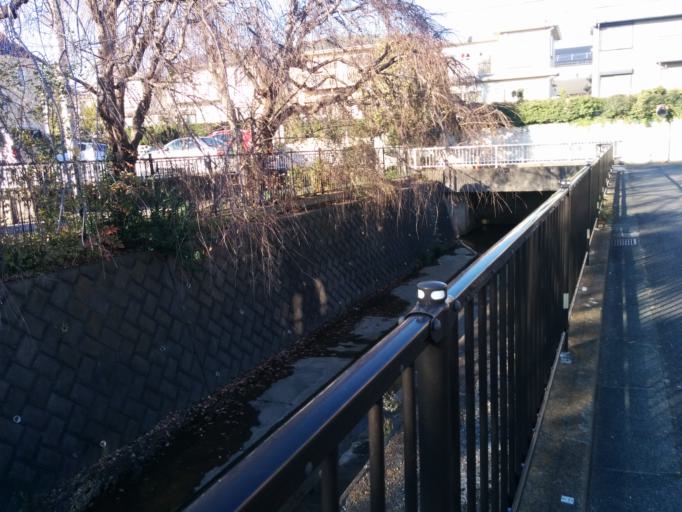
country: JP
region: Kanagawa
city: Fujisawa
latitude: 35.3744
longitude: 139.4398
